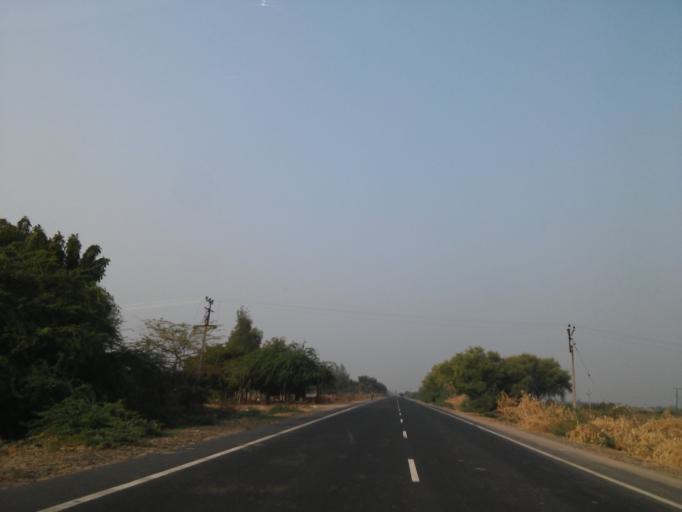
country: IN
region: Gujarat
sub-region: Kachchh
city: Anjar
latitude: 23.2887
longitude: 70.0179
